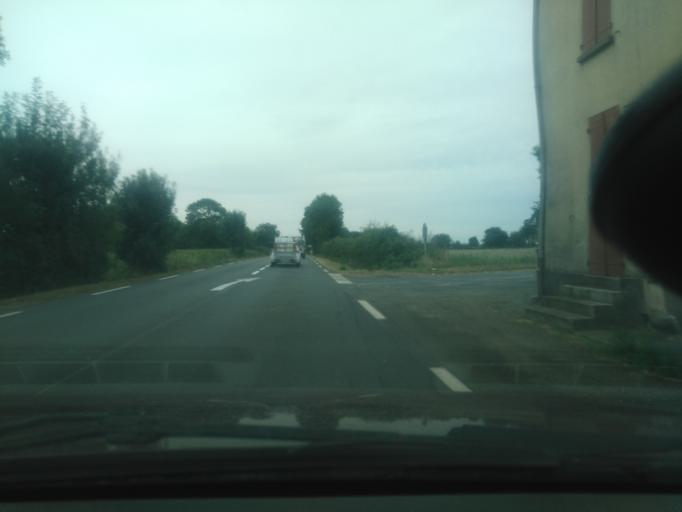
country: FR
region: Pays de la Loire
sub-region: Departement de la Vendee
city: Bazoges-en-Pareds
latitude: 46.6794
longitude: -0.9458
